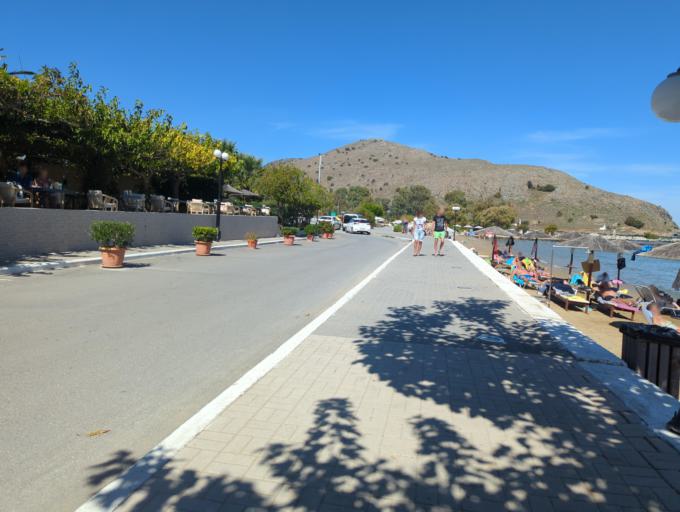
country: GR
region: Crete
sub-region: Nomos Chanias
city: Georgioupolis
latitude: 35.3632
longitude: 24.2621
